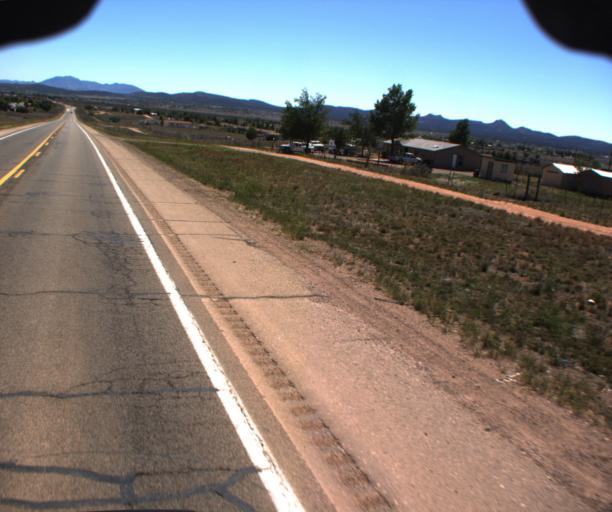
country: US
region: Arizona
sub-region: Yavapai County
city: Paulden
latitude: 34.9065
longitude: -112.4625
